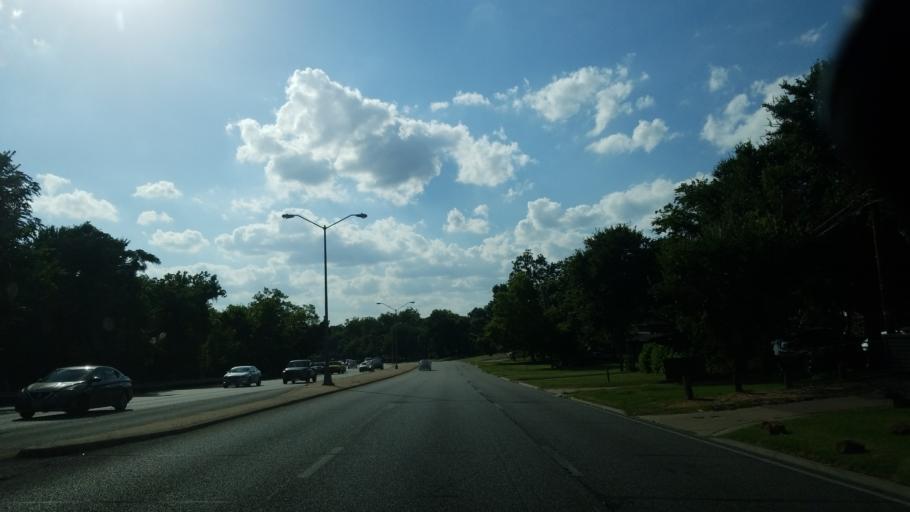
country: US
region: Texas
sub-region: Dallas County
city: Dallas
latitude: 32.7644
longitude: -96.7132
